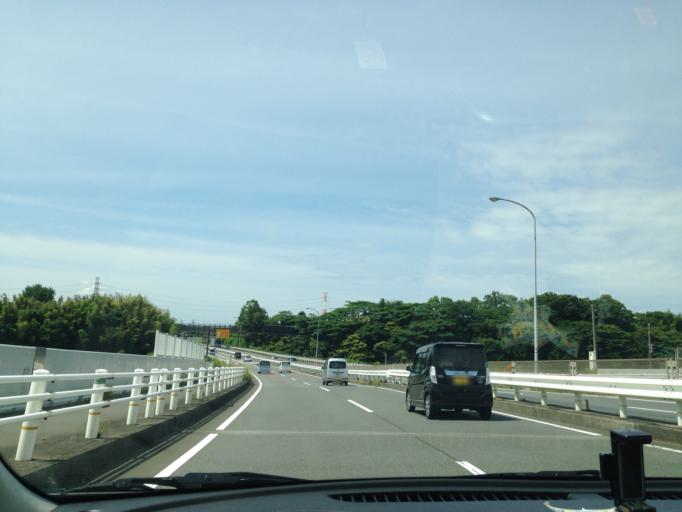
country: JP
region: Shizuoka
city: Mishima
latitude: 35.1468
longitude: 138.8877
